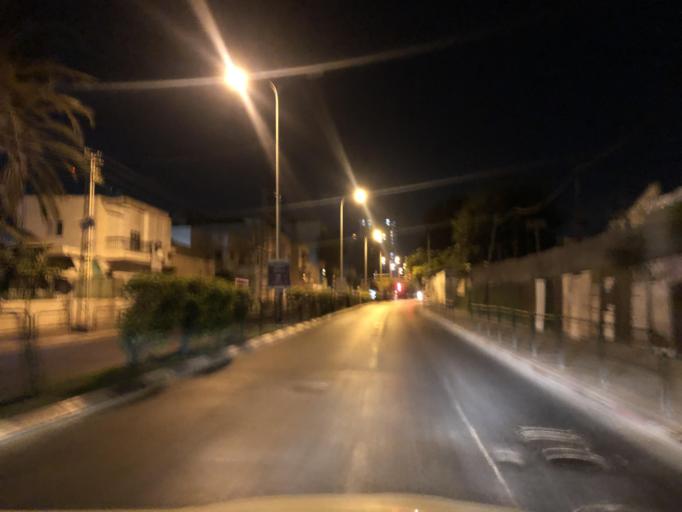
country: IL
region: Tel Aviv
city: Azor
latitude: 32.0476
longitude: 34.7947
